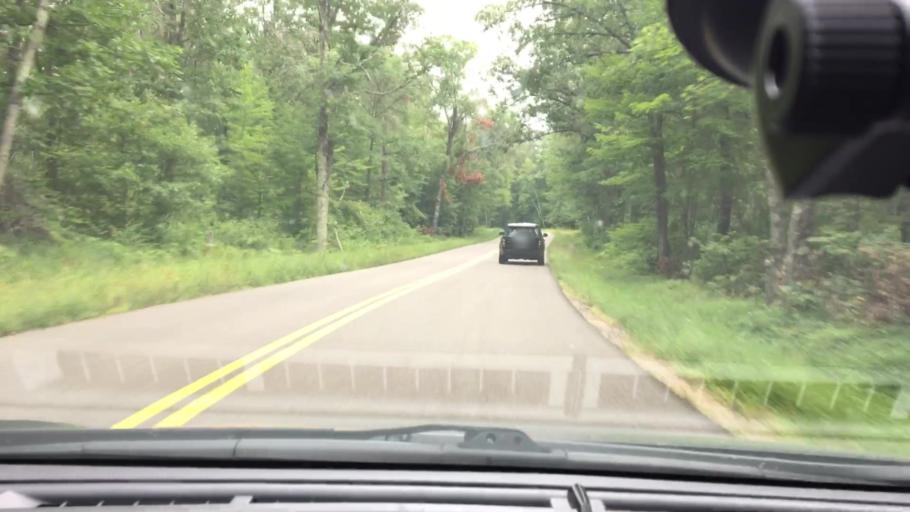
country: US
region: Minnesota
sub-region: Crow Wing County
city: Cross Lake
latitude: 46.6676
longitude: -94.0419
